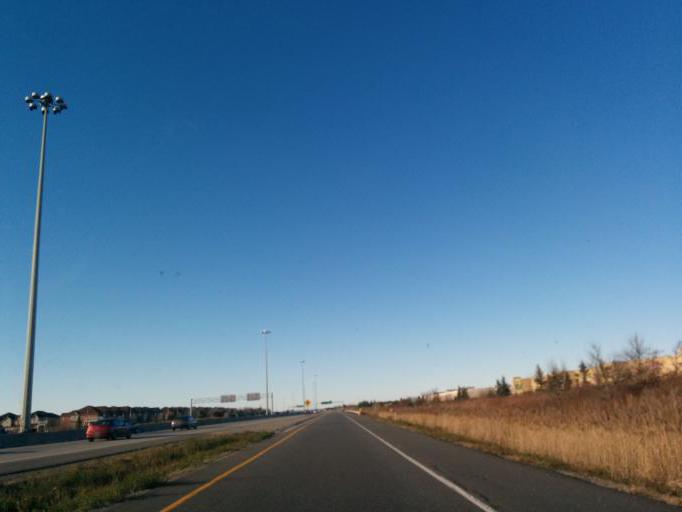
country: CA
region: Ontario
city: Brampton
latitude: 43.7280
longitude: -79.7667
